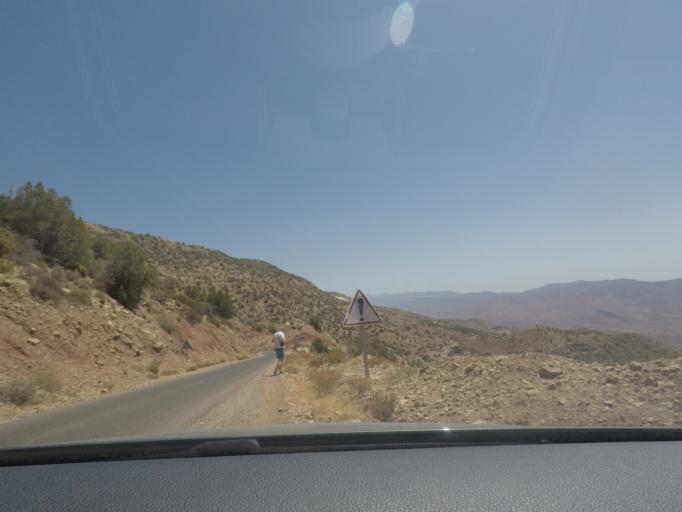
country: MA
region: Souss-Massa-Draa
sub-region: Taroudannt
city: Bigoudine
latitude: 30.7466
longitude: -9.2790
